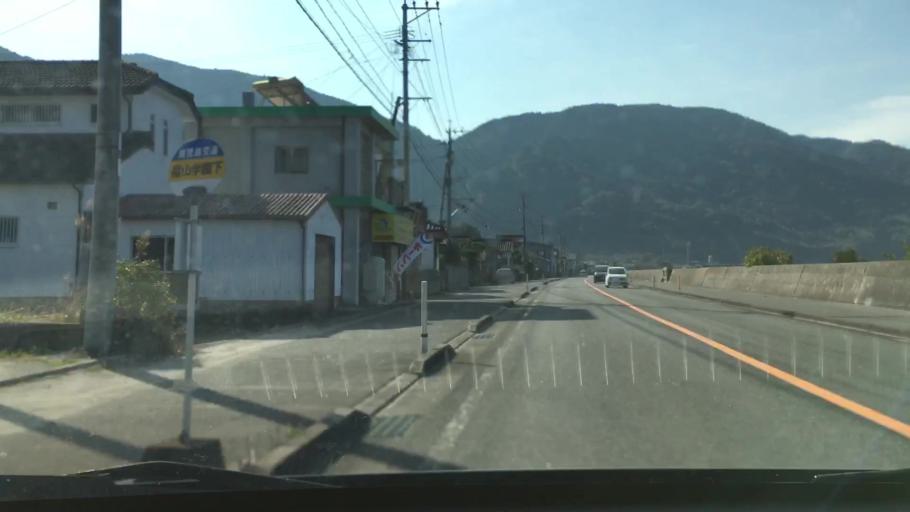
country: JP
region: Kagoshima
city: Kokubu-matsuki
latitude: 31.6548
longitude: 130.8230
